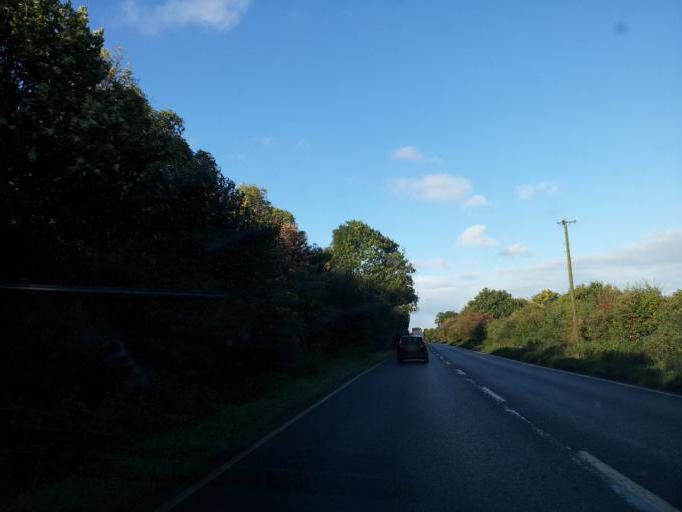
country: GB
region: England
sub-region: Norfolk
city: King's Lynn
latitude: 52.7159
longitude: 0.4742
